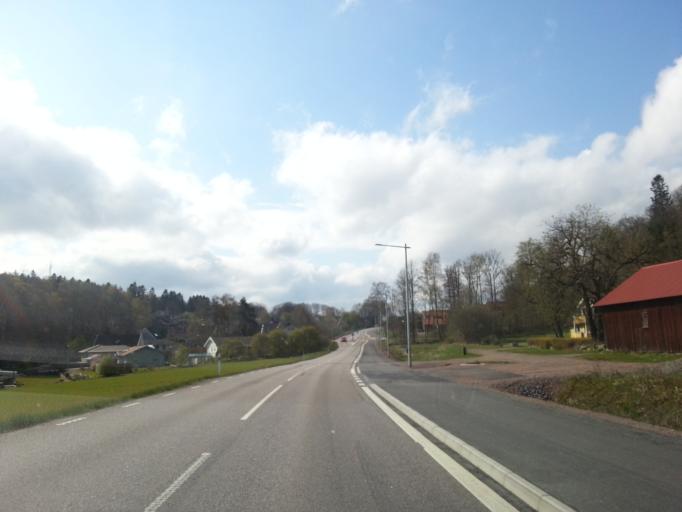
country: SE
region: Vaestra Goetaland
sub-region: Ale Kommun
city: Surte
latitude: 57.8078
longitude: 11.9971
